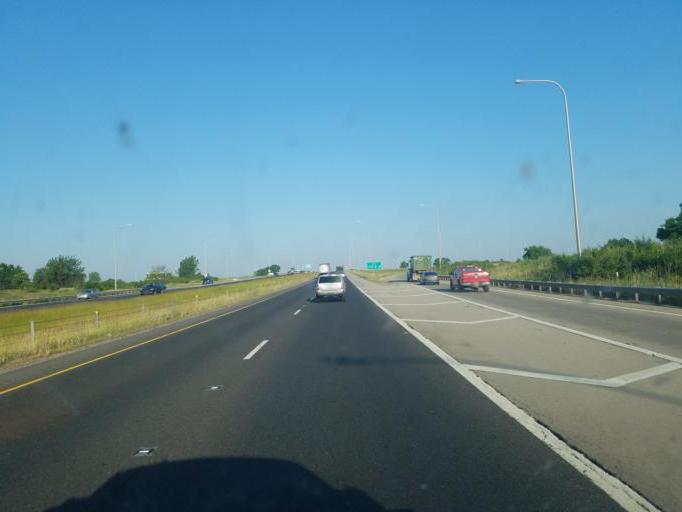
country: US
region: Illinois
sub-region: Will County
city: Shorewood
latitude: 41.4867
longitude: -88.1892
